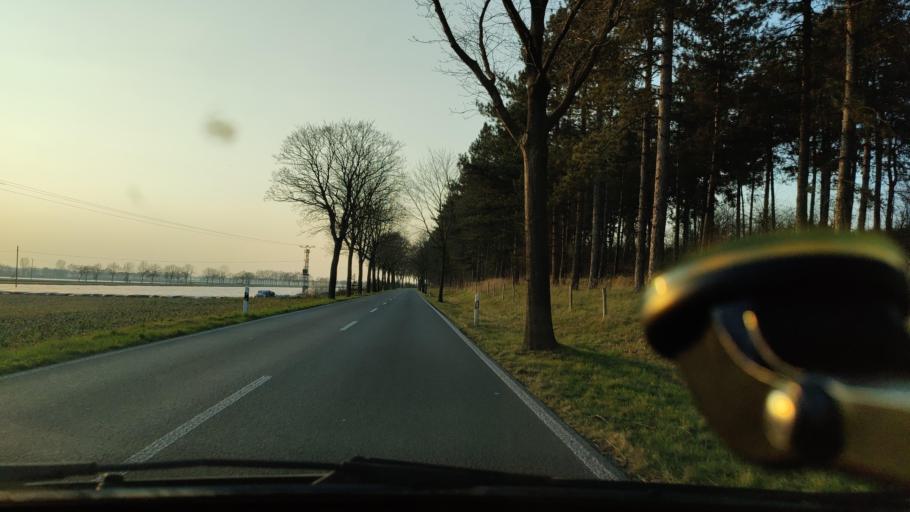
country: NL
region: Limburg
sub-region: Gemeente Bergen
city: Wellerlooi
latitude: 51.5968
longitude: 6.1210
